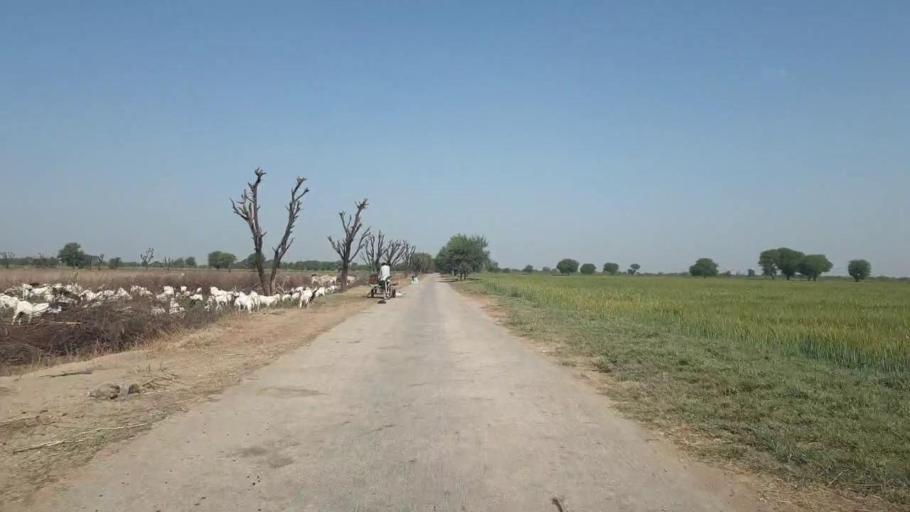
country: PK
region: Sindh
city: Umarkot
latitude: 25.2859
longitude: 69.6406
